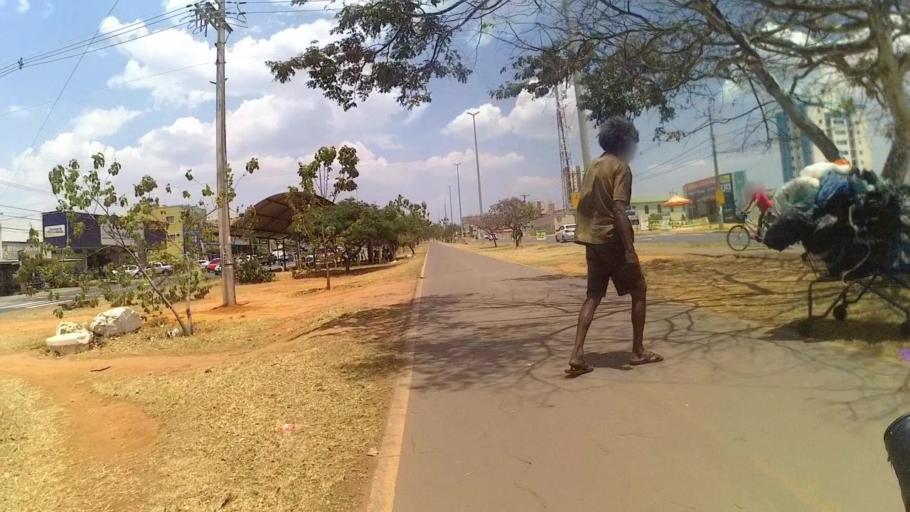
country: BR
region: Federal District
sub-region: Brasilia
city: Brasilia
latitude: -15.8732
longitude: -48.0714
